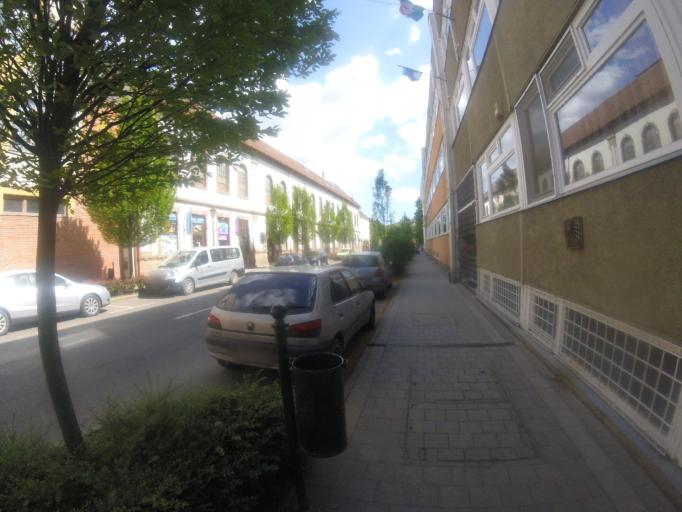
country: HU
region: Bekes
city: Gyula
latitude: 46.6458
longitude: 21.2769
